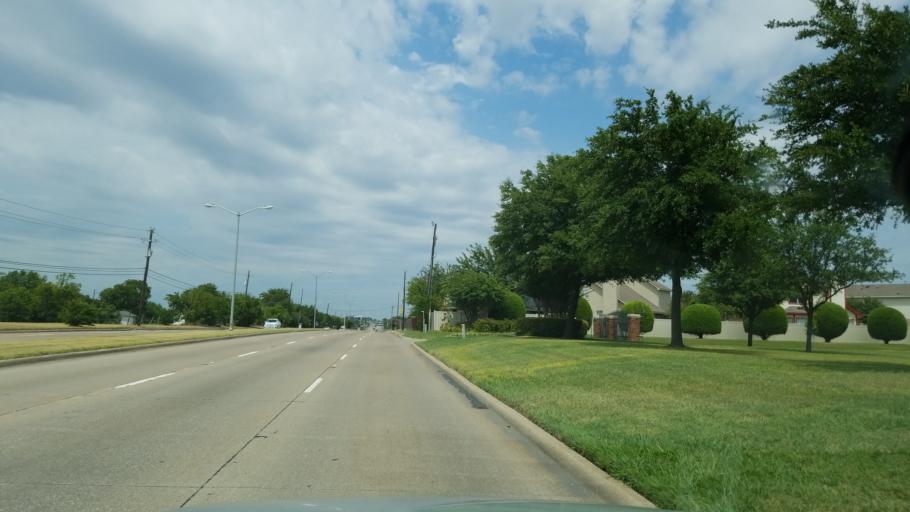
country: US
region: Texas
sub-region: Dallas County
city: Duncanville
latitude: 32.6557
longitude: -96.8570
